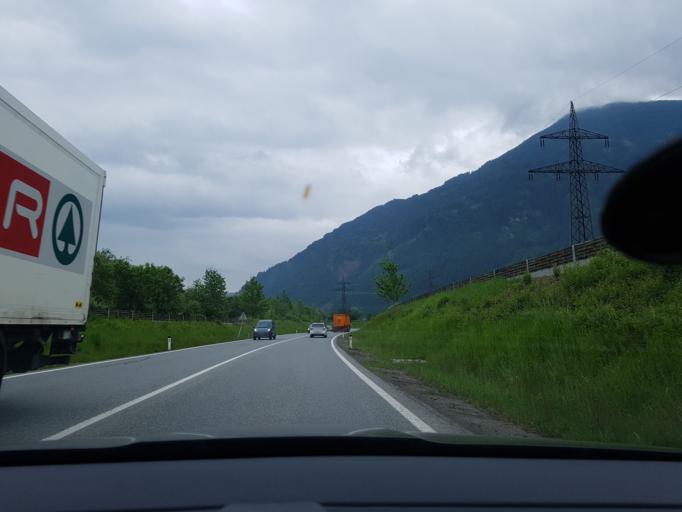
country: AT
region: Tyrol
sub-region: Politischer Bezirk Schwaz
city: Ried im Zillertal
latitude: 47.2955
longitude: 11.8763
